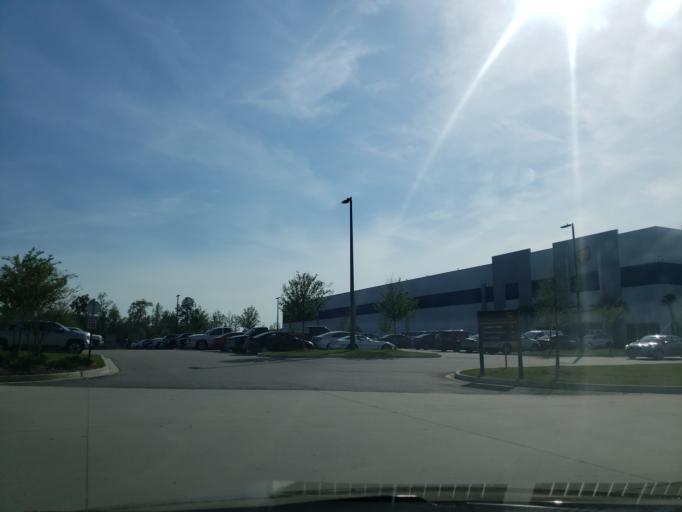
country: US
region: Georgia
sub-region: Chatham County
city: Garden City
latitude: 32.1012
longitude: -81.1854
